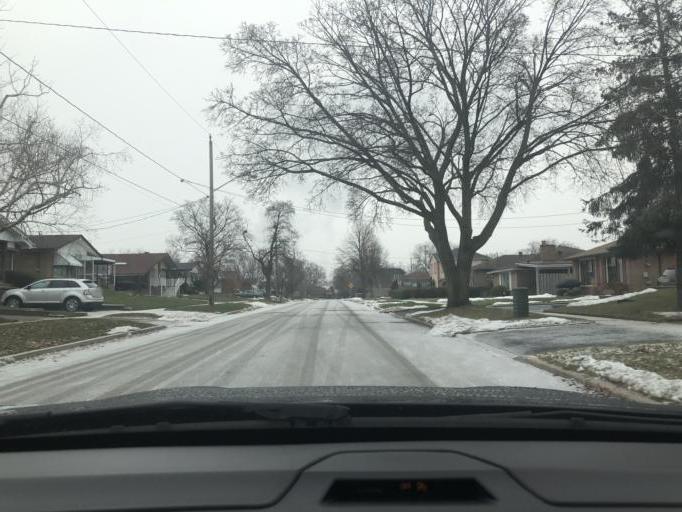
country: CA
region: Ontario
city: Scarborough
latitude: 43.7813
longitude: -79.2711
